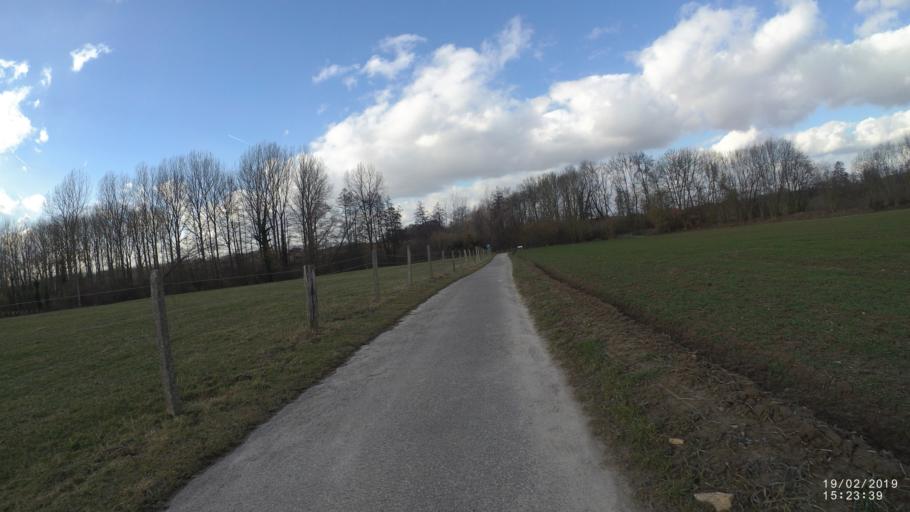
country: BE
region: Flanders
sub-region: Provincie Limburg
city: Tongeren
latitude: 50.7969
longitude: 5.4101
